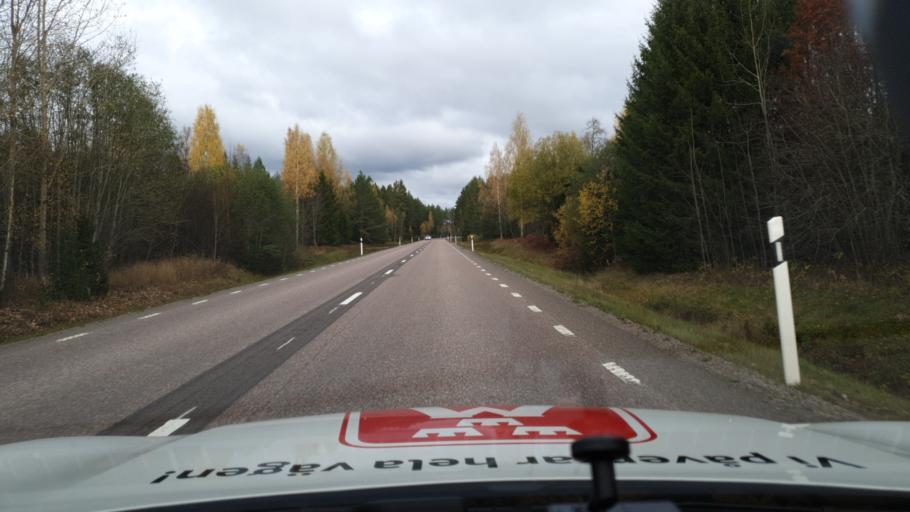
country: SE
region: Gaevleborg
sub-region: Gavle Kommun
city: Hedesunda
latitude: 60.4011
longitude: 16.9745
